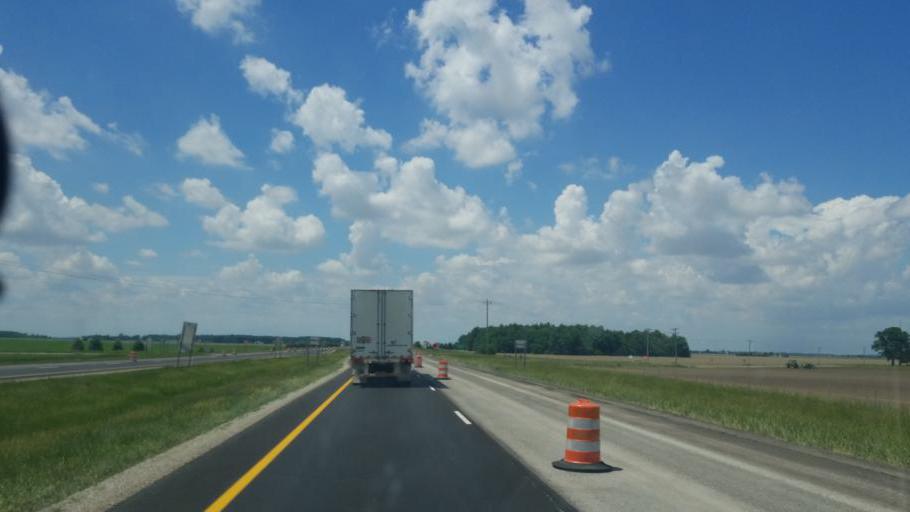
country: US
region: Ohio
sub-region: Van Wert County
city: Convoy
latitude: 40.9644
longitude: -84.7444
